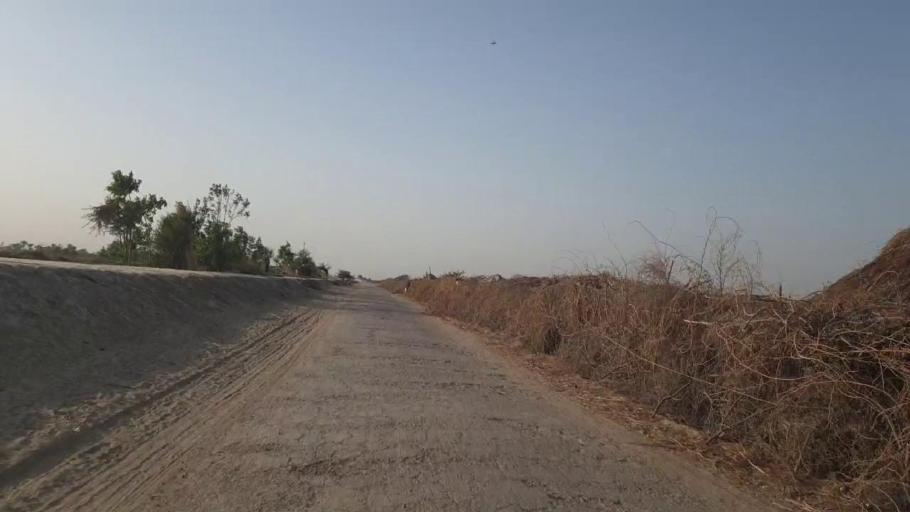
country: PK
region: Sindh
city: Dhoro Naro
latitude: 25.4905
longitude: 69.5670
